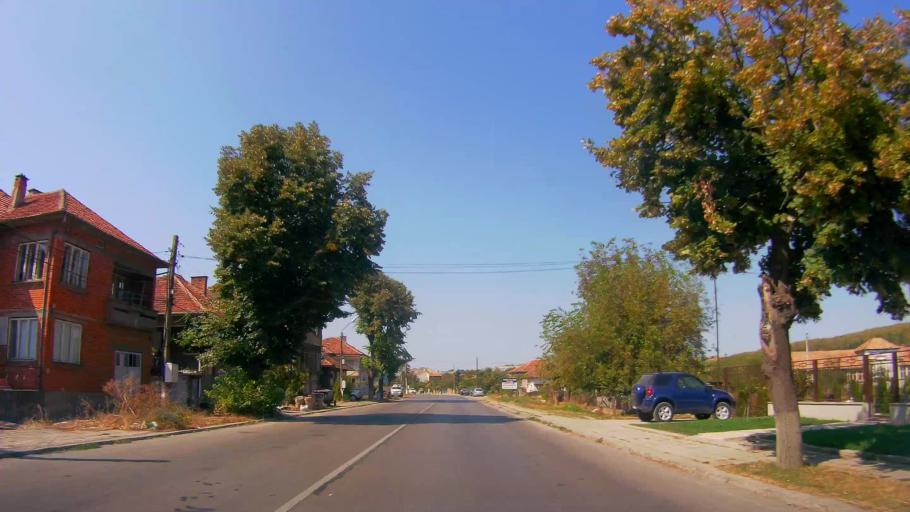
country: BG
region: Razgrad
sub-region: Obshtina Tsar Kaloyan
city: Tsar Kaloyan
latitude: 43.6102
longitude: 26.2341
